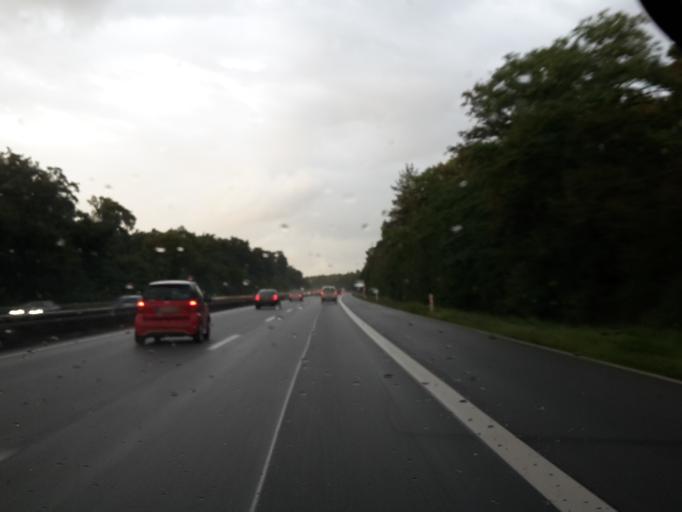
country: DE
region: Hesse
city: Raunheim
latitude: 50.0022
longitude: 8.4805
